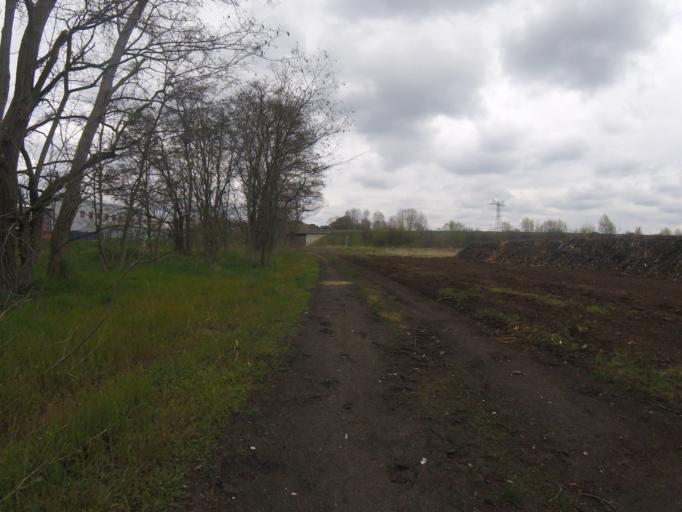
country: DE
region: Brandenburg
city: Mittenwalde
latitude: 52.2602
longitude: 13.5775
